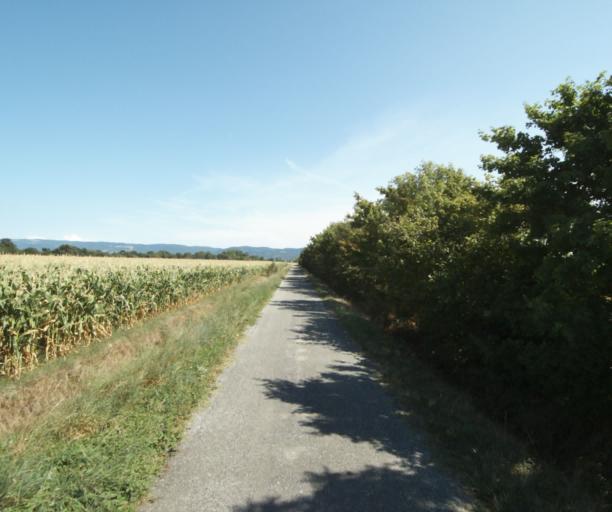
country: FR
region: Midi-Pyrenees
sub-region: Departement de la Haute-Garonne
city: Revel
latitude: 43.4863
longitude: 1.9740
